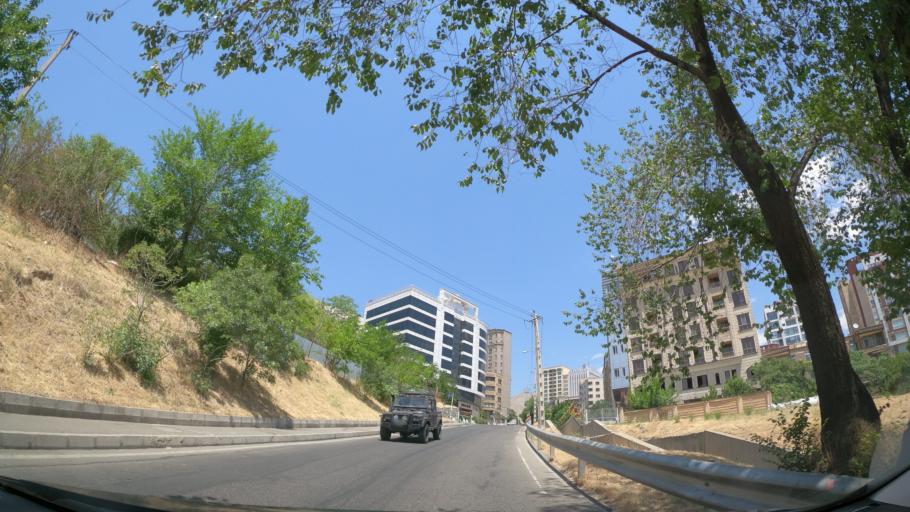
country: IR
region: Tehran
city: Tajrish
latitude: 35.7798
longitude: 51.3868
